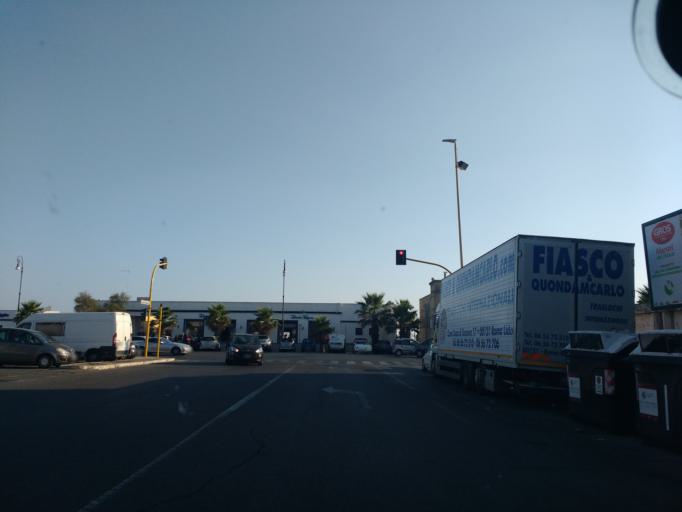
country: IT
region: Latium
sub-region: Citta metropolitana di Roma Capitale
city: Lido di Ostia
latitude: 41.7314
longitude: 12.2727
